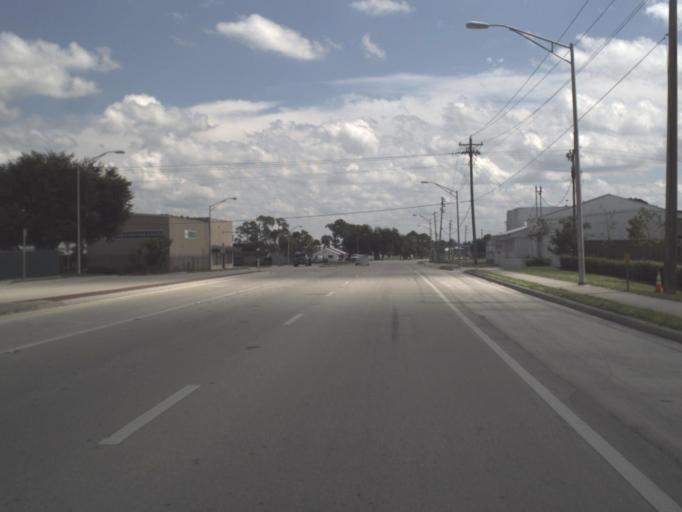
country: US
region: Florida
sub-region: Collier County
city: Immokalee
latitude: 26.4185
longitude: -81.4142
